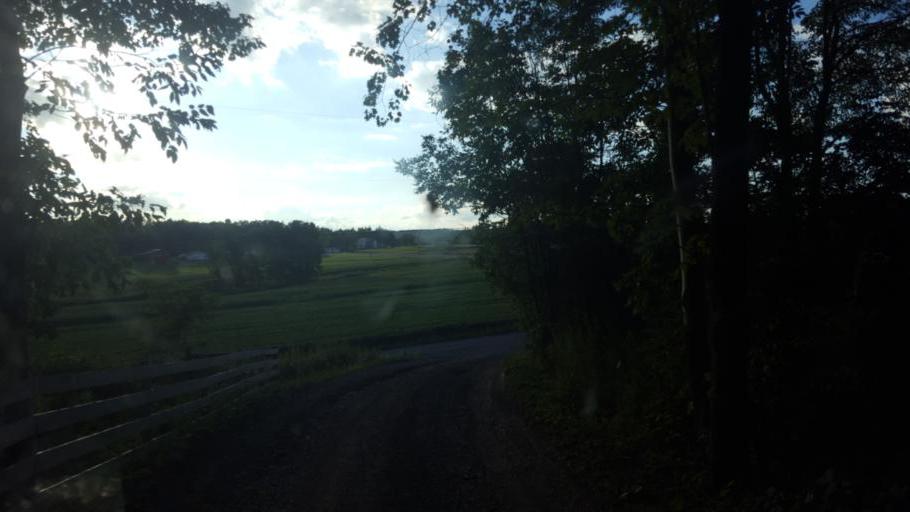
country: US
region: Pennsylvania
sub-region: Clarion County
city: Knox
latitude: 41.2325
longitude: -79.5685
